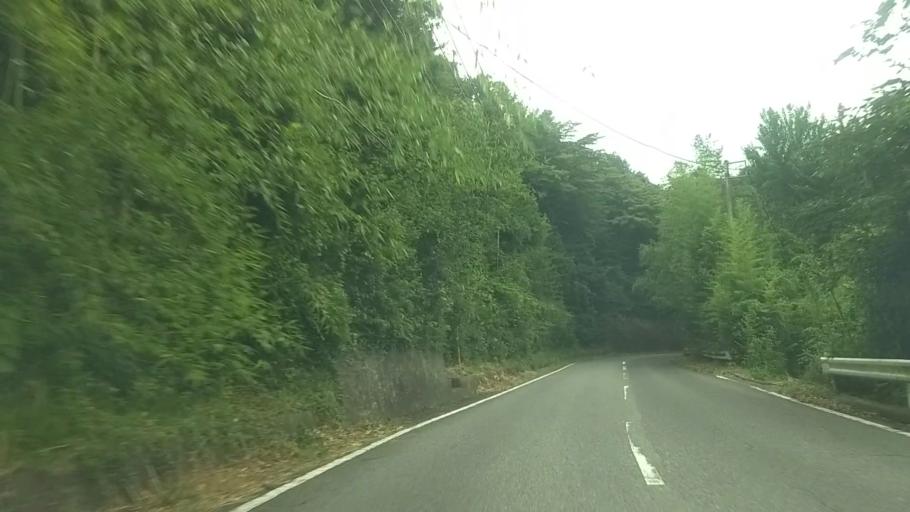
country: JP
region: Chiba
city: Kimitsu
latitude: 35.2321
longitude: 140.0094
